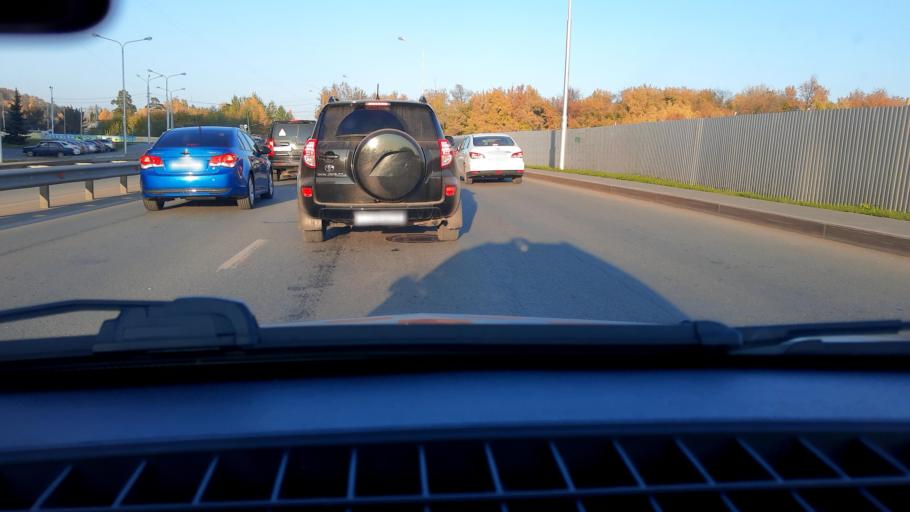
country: RU
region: Bashkortostan
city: Ufa
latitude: 54.8017
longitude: 56.1349
